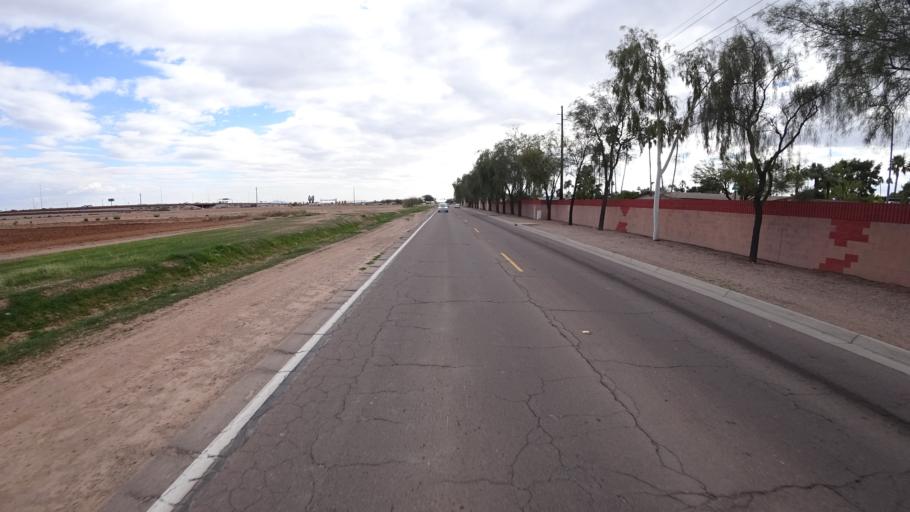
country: US
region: Arizona
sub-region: Maricopa County
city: Scottsdale
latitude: 33.4988
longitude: -111.8917
